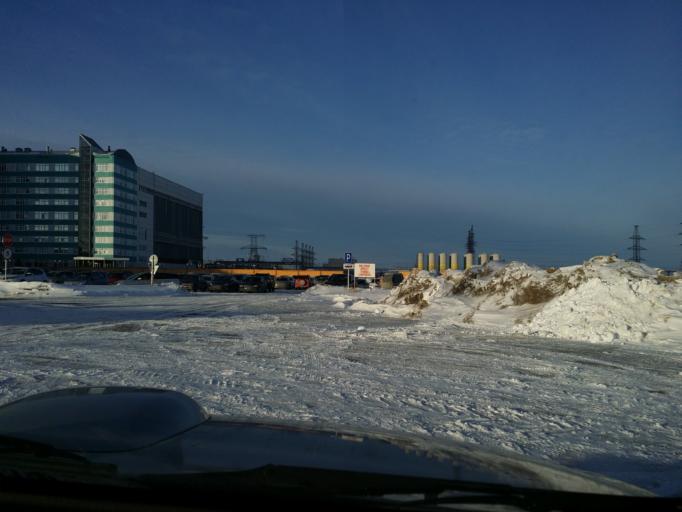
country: RU
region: Khanty-Mansiyskiy Avtonomnyy Okrug
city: Izluchinsk
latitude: 60.9742
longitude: 76.9471
